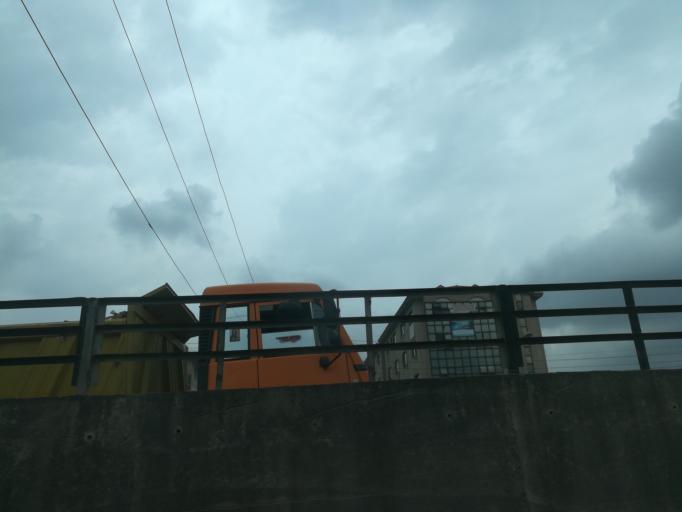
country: NG
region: Lagos
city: Ojota
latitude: 6.6048
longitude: 3.3913
